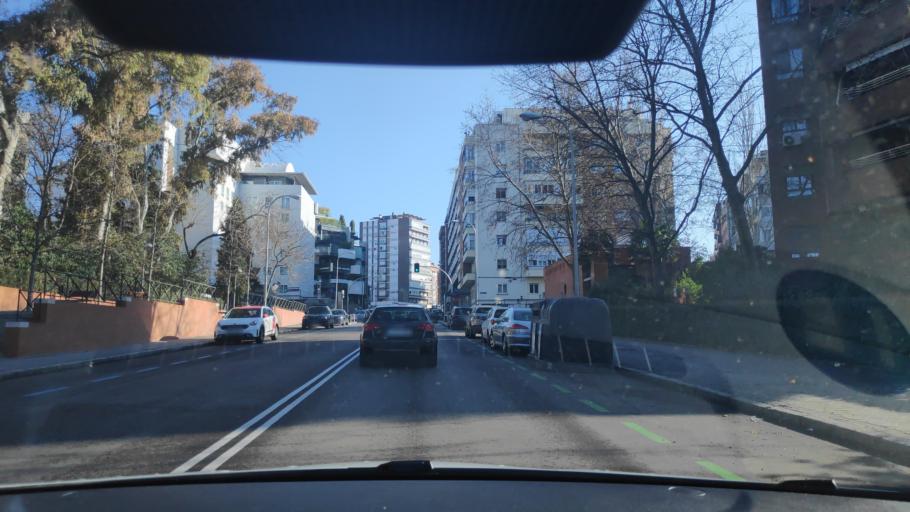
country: ES
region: Madrid
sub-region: Provincia de Madrid
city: Chamartin
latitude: 40.4550
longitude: -3.6827
